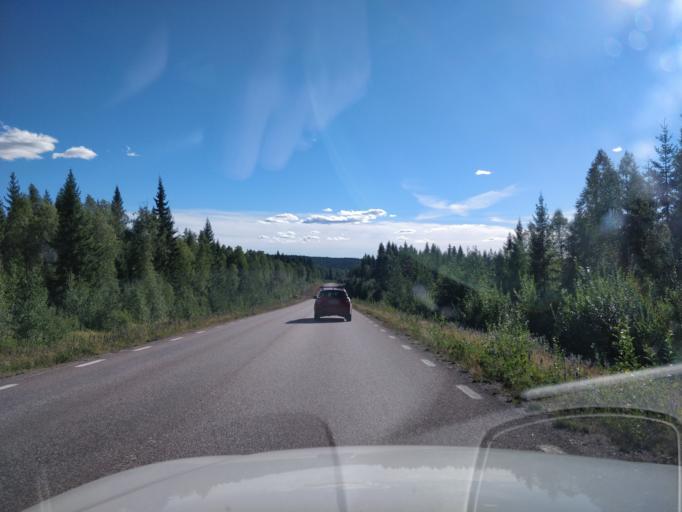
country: SE
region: Vaermland
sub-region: Filipstads Kommun
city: Lesjofors
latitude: 60.1488
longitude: 14.4273
